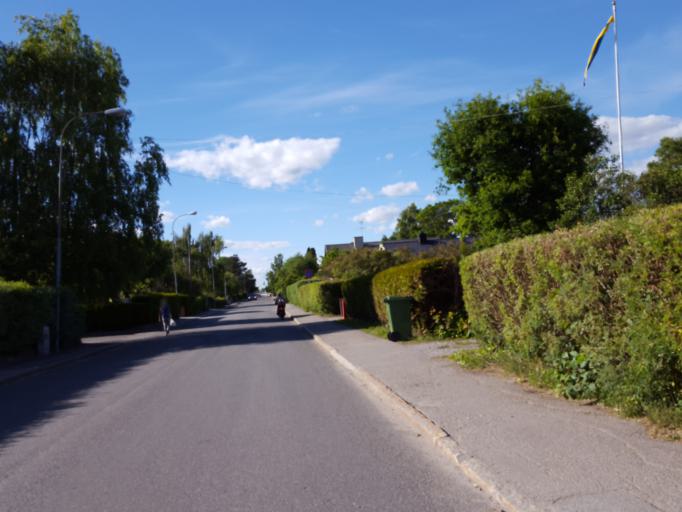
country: SE
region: Stockholm
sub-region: Sollentuna Kommun
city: Sollentuna
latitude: 59.4325
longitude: 17.9395
